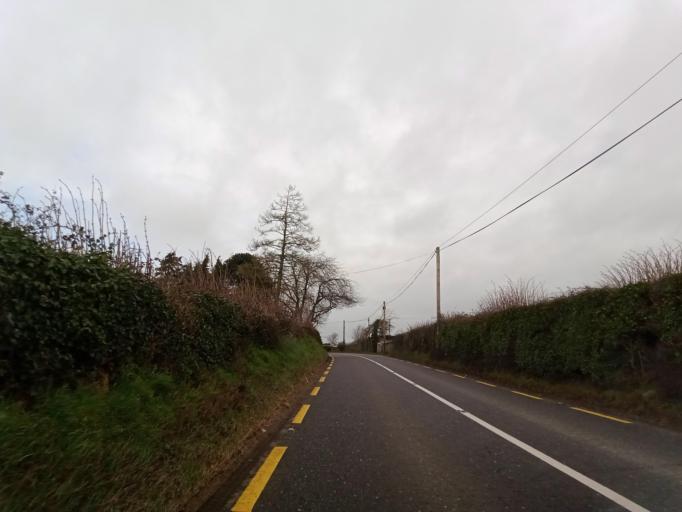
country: IE
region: Leinster
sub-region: Kilkenny
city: Kilkenny
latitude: 52.7174
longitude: -7.2929
